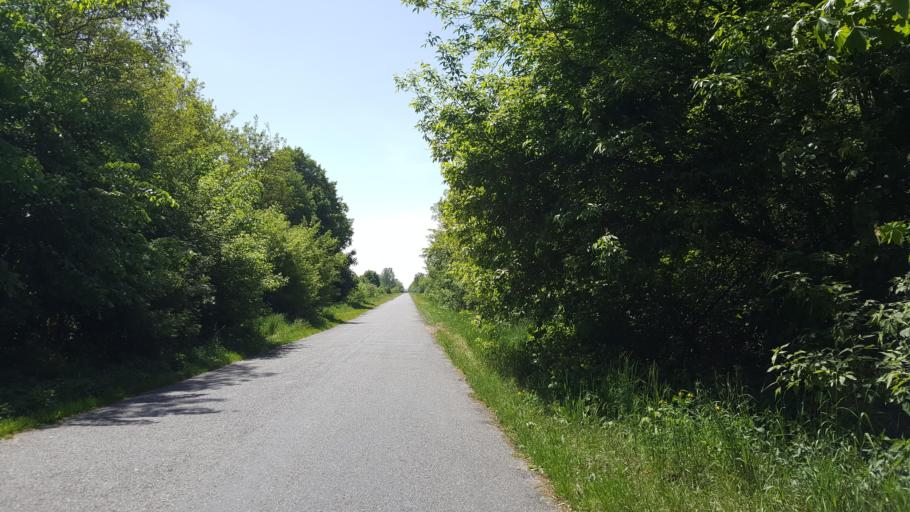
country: BY
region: Brest
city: Charnawchytsy
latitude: 52.2345
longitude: 23.7436
